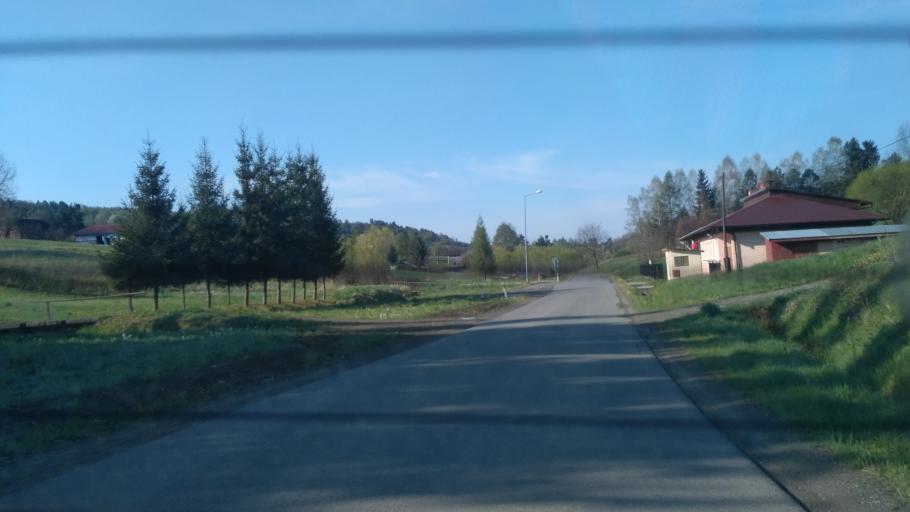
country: PL
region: Subcarpathian Voivodeship
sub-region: Powiat jaroslawski
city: Kramarzowka
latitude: 49.8270
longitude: 22.4990
